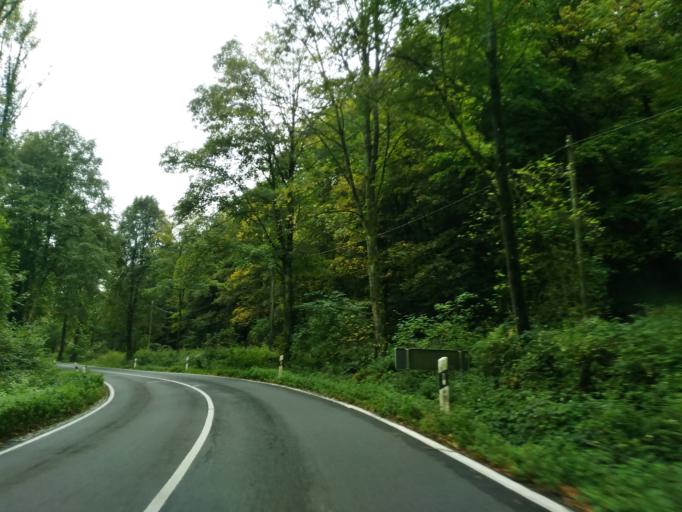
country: DE
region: North Rhine-Westphalia
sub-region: Regierungsbezirk Koln
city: Bad Honnef
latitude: 50.6493
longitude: 7.2455
